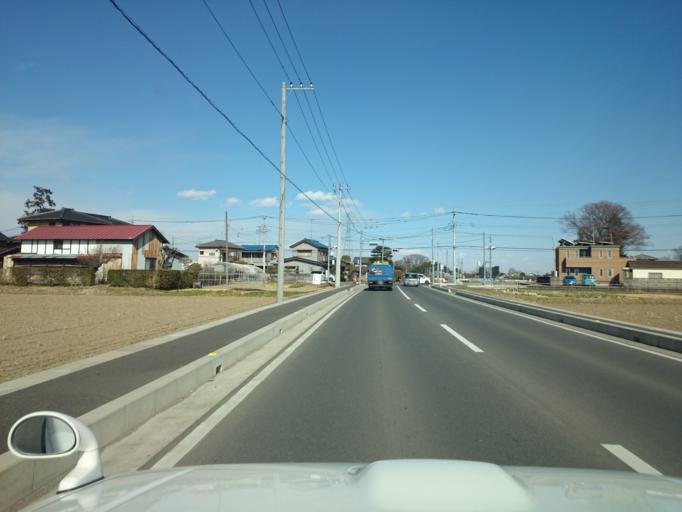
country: JP
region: Saitama
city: Satte
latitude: 36.0526
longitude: 139.7261
